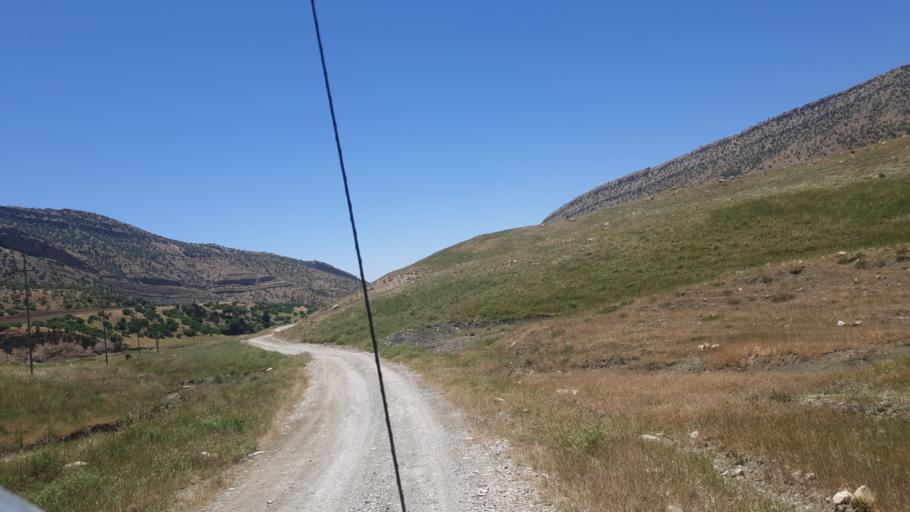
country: IQ
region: Arbil
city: Nahiyat Hiran
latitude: 36.1973
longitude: 44.4213
